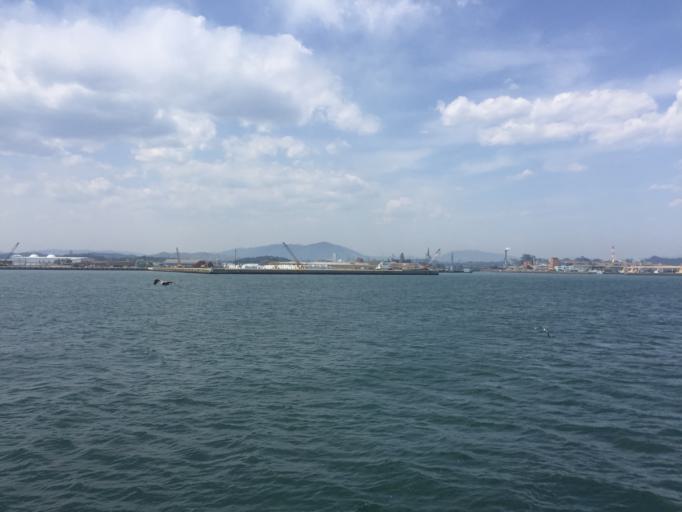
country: JP
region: Fukushima
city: Iwaki
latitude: 36.9241
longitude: 140.8771
